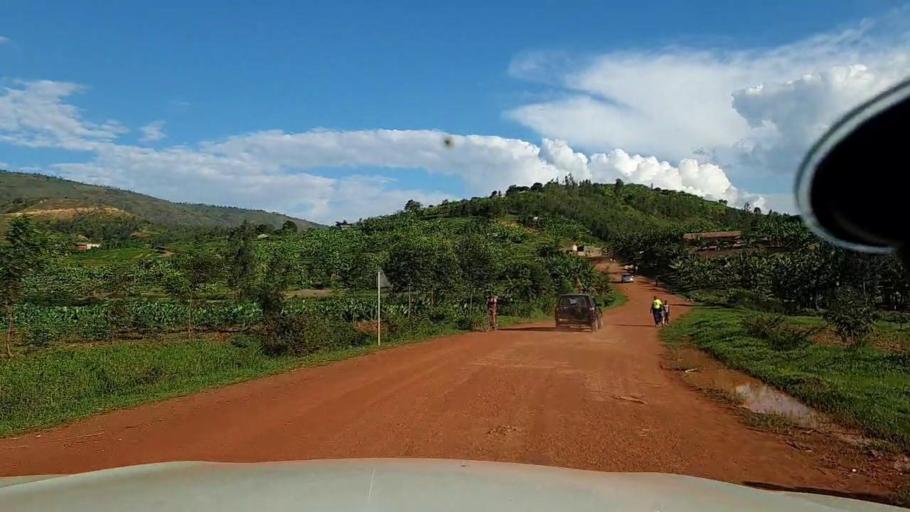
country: RW
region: Kigali
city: Kigali
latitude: -1.8640
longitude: 29.9296
